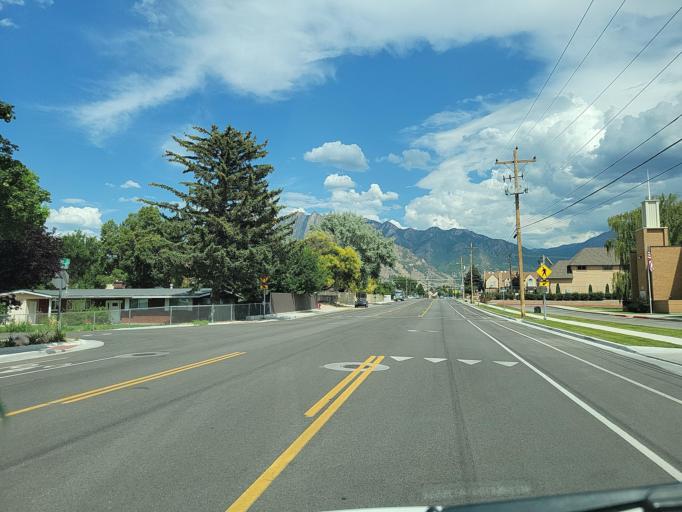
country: US
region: Utah
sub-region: Salt Lake County
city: Murray
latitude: 40.6406
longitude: -111.8585
